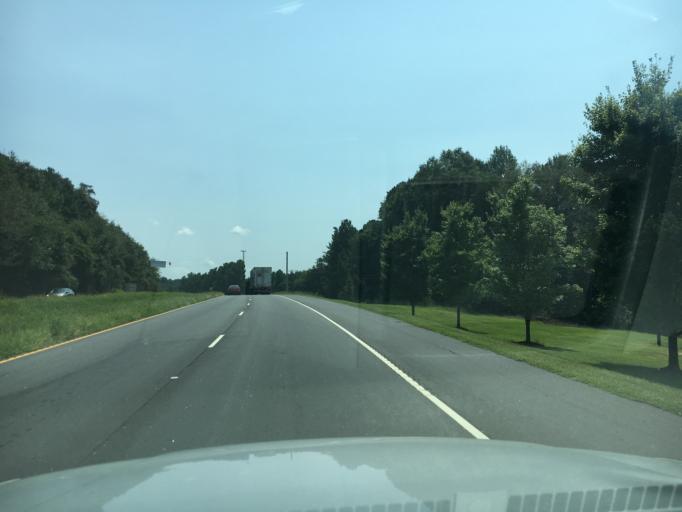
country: US
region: South Carolina
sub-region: Pickens County
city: Clemson
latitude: 34.6620
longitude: -82.8142
